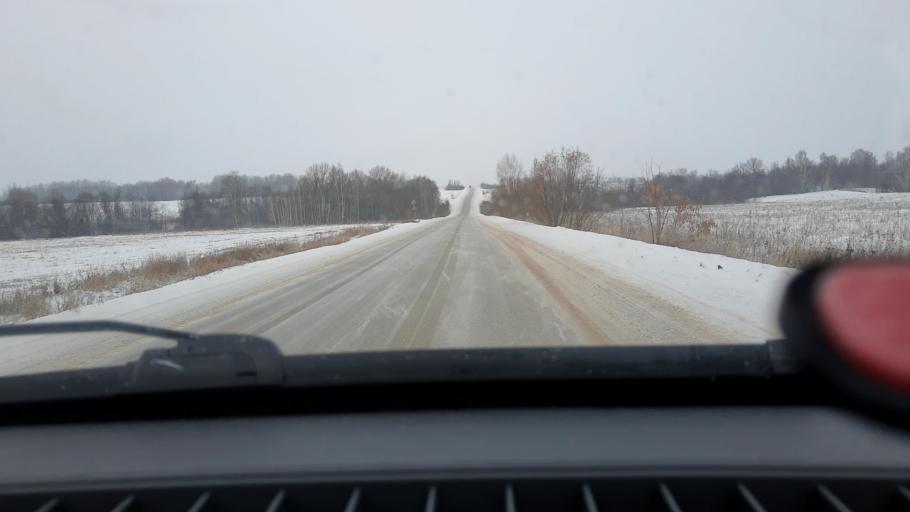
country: RU
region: Bashkortostan
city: Iglino
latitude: 54.6991
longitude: 56.4169
